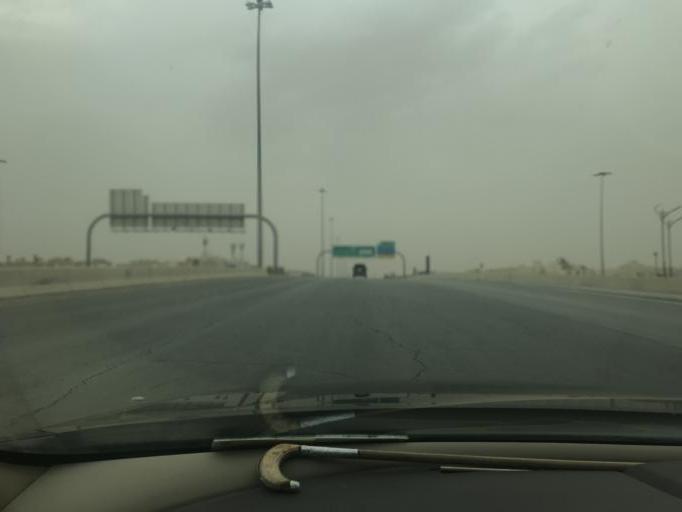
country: SA
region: Ar Riyad
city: Riyadh
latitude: 24.7841
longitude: 46.7050
